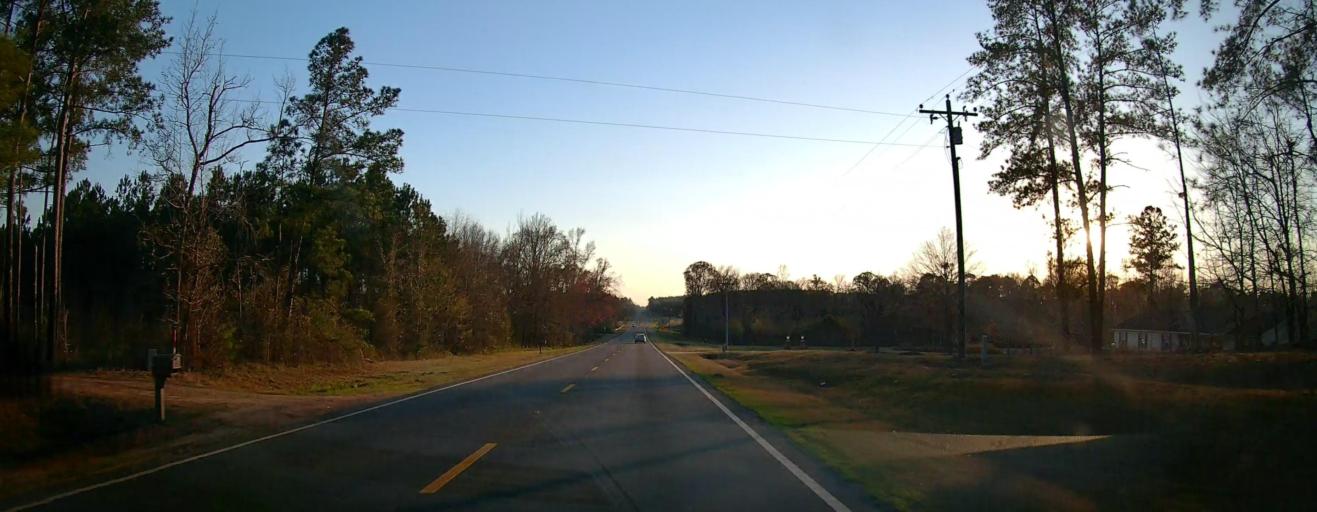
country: US
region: Georgia
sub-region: Laurens County
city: Dublin
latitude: 32.4063
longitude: -82.9656
